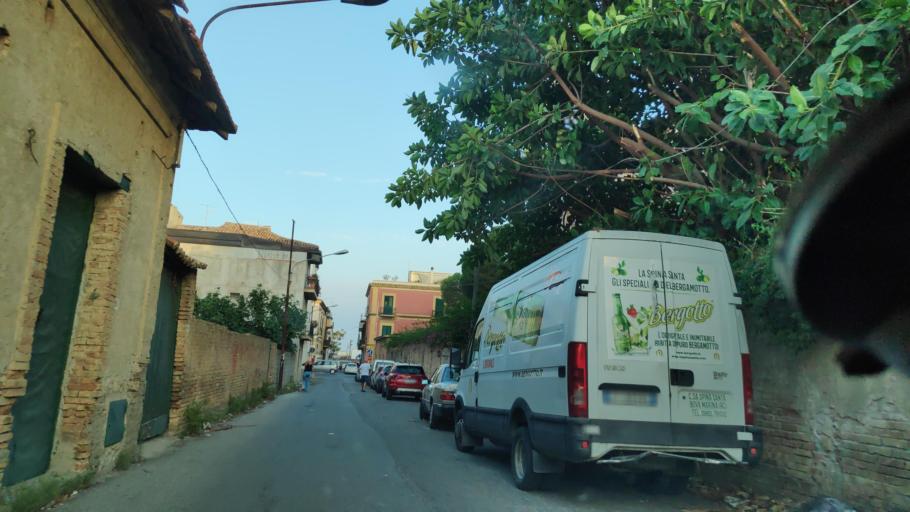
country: IT
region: Calabria
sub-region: Provincia di Reggio Calabria
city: Siderno
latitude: 38.2663
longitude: 16.2942
